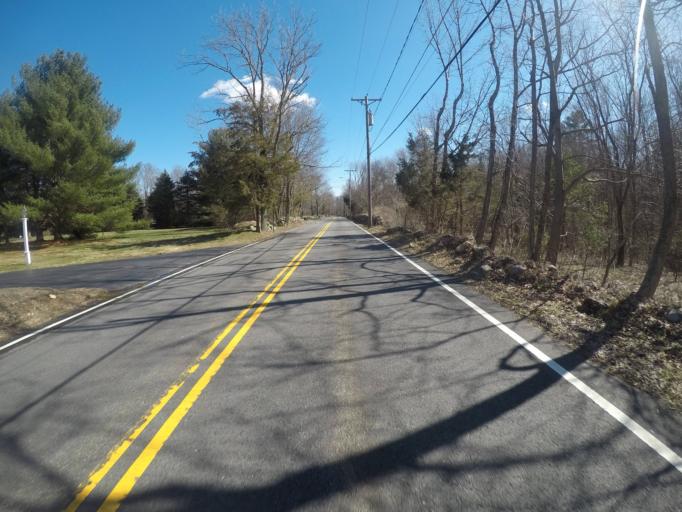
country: US
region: Massachusetts
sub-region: Bristol County
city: Easton
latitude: 42.0453
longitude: -71.1422
